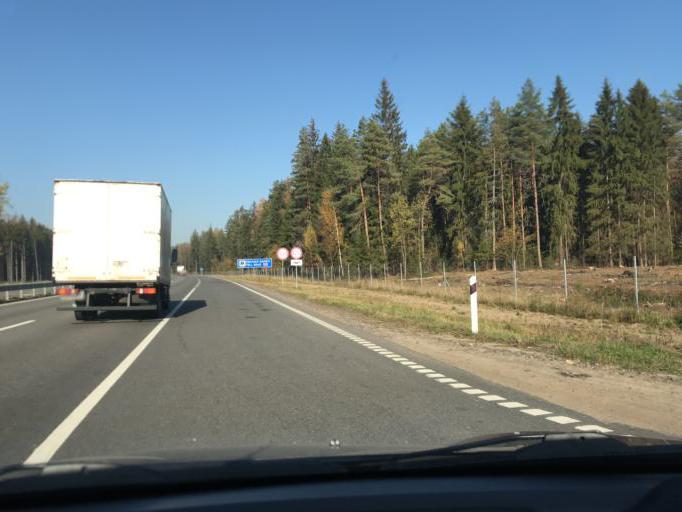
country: BY
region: Mogilev
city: Kirawsk
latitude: 53.2190
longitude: 29.3412
